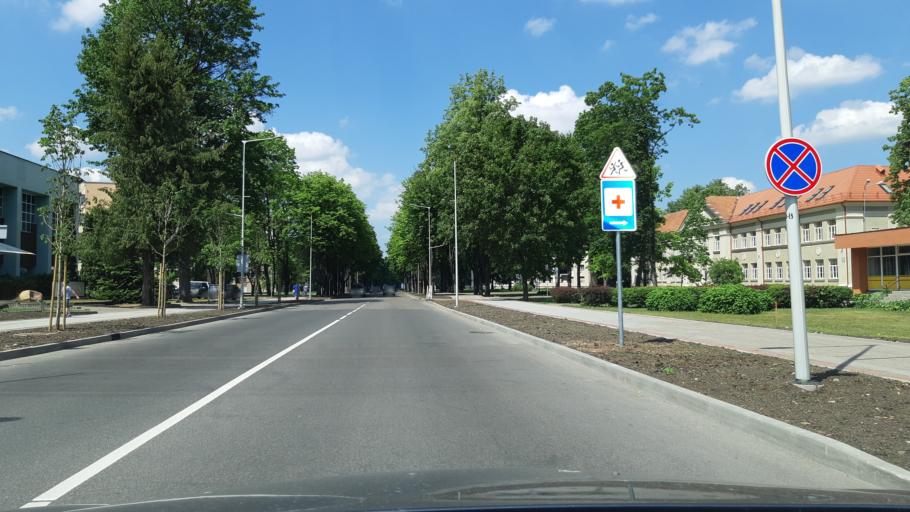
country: LT
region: Alytaus apskritis
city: Druskininkai
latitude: 54.0127
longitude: 23.9872
